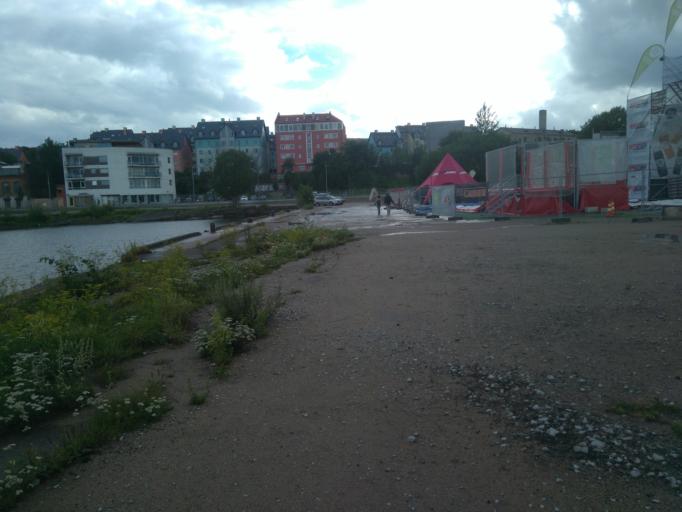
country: EE
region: Harju
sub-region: Tallinna linn
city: Tallinn
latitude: 59.4467
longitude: 24.7486
